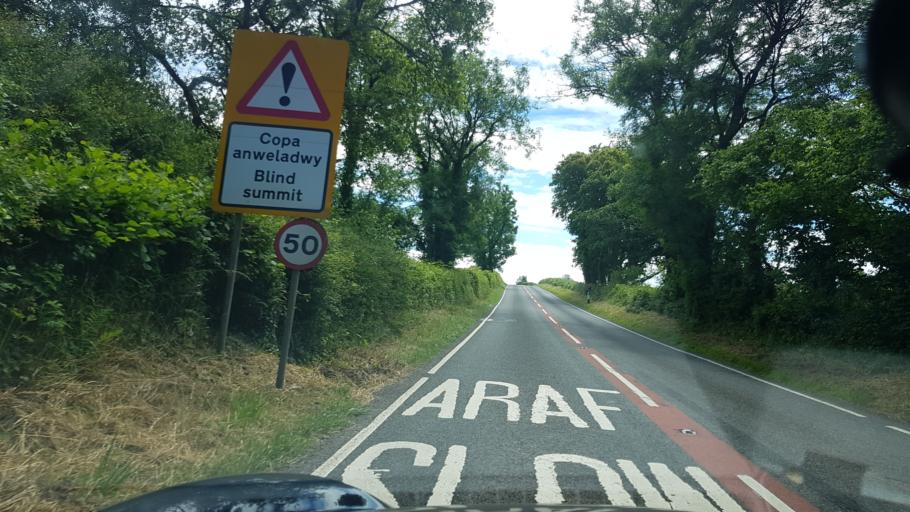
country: GB
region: Wales
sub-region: Carmarthenshire
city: Saint Clears
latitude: 51.7952
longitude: -4.4859
